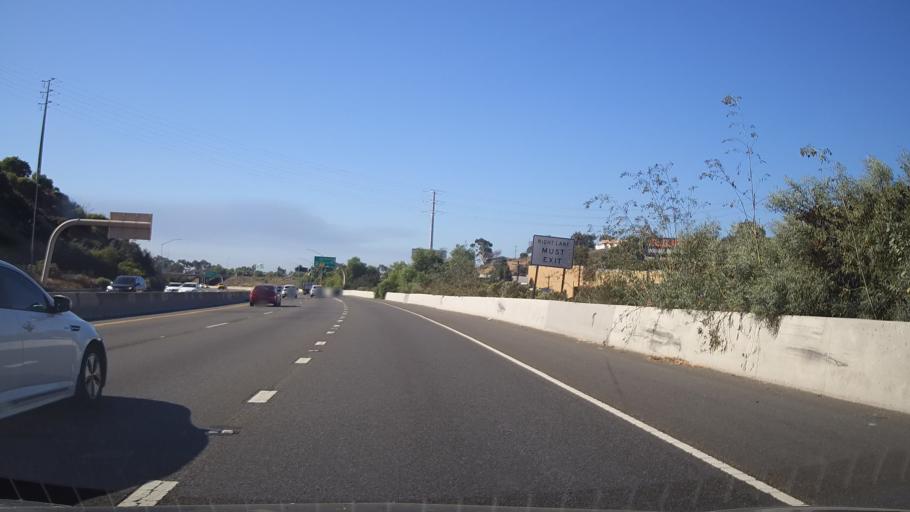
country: US
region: California
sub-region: San Diego County
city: San Diego
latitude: 32.7216
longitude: -117.1172
